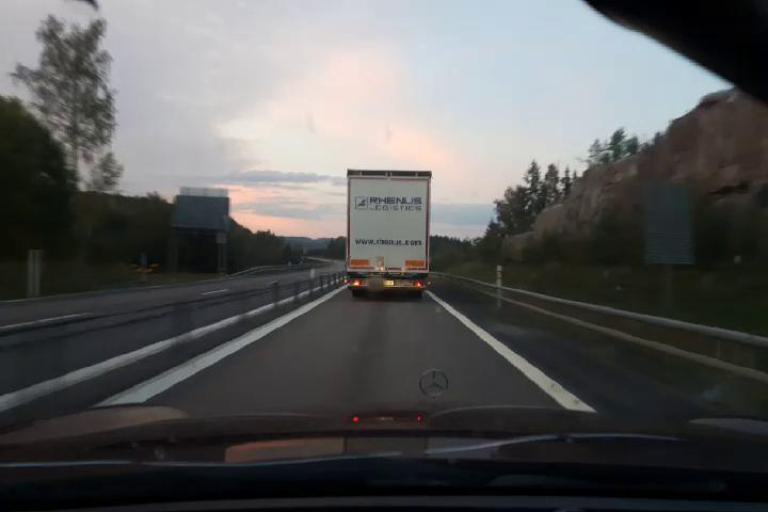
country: SE
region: Vaesternorrland
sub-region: Haernoesands Kommun
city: Haernoesand
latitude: 62.8185
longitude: 17.9694
